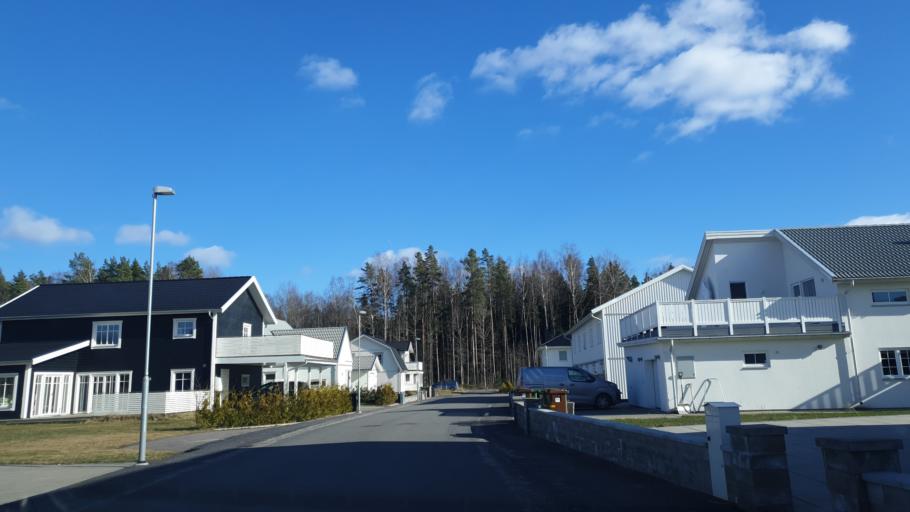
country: SE
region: OErebro
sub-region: Orebro Kommun
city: Orebro
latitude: 59.3030
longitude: 15.1646
